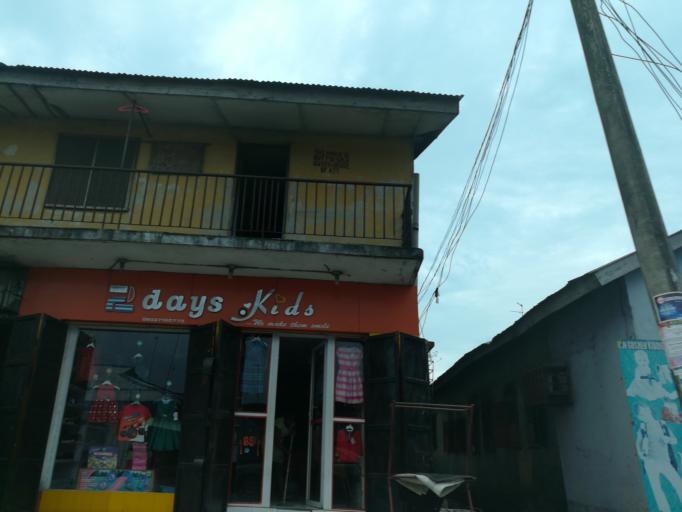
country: NG
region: Rivers
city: Port Harcourt
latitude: 4.7942
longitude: 6.9993
